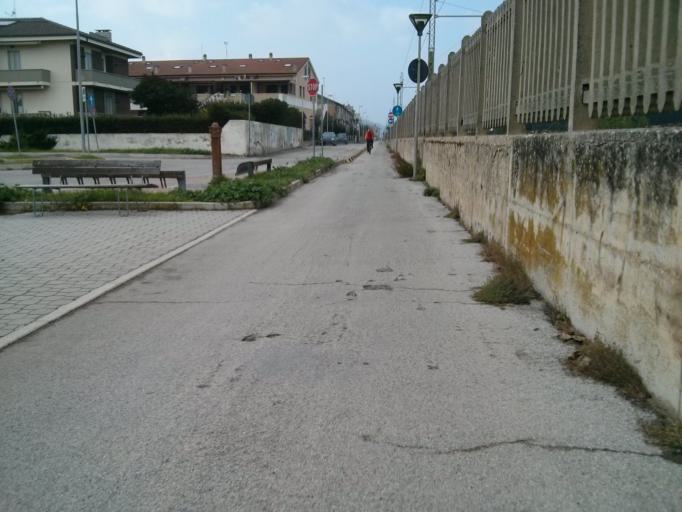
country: IT
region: The Marches
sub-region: Provincia di Pesaro e Urbino
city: Fano
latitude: 43.8577
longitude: 12.9987
